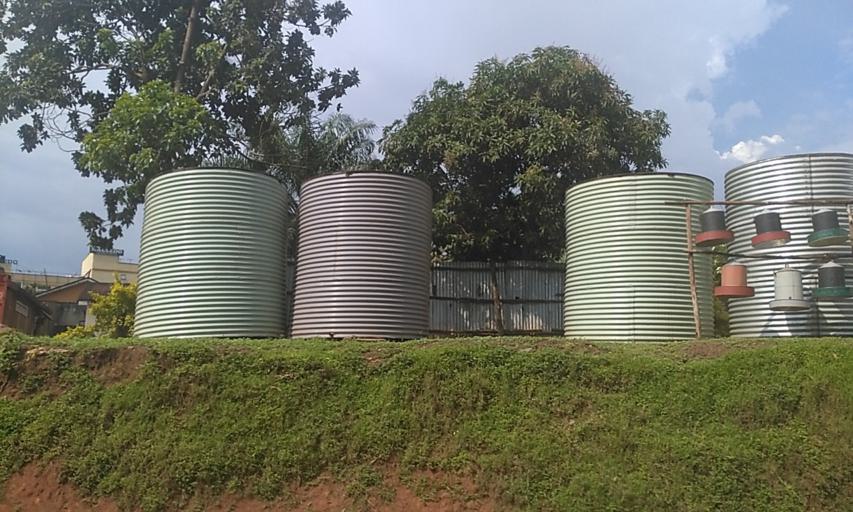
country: UG
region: Central Region
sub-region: Kampala District
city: Kampala
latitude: 0.2944
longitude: 32.5560
